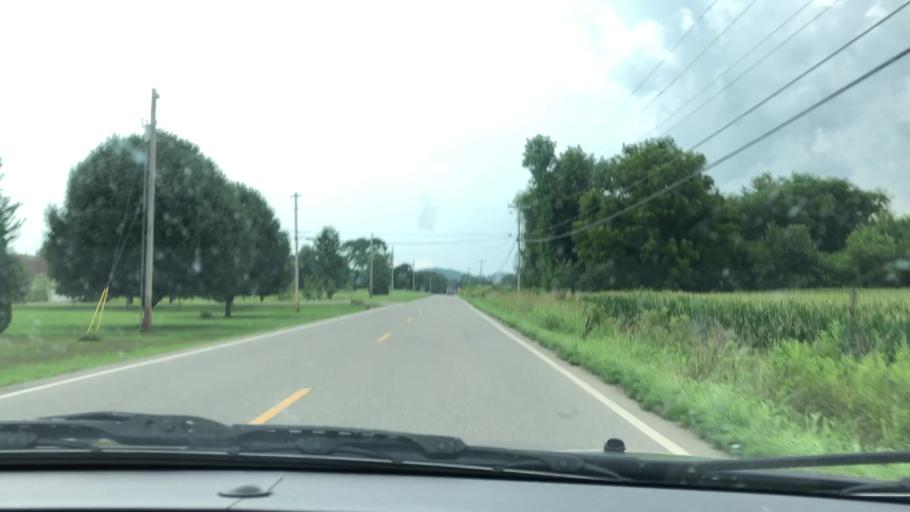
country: US
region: Tennessee
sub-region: Maury County
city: Spring Hill
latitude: 35.7705
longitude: -87.0063
